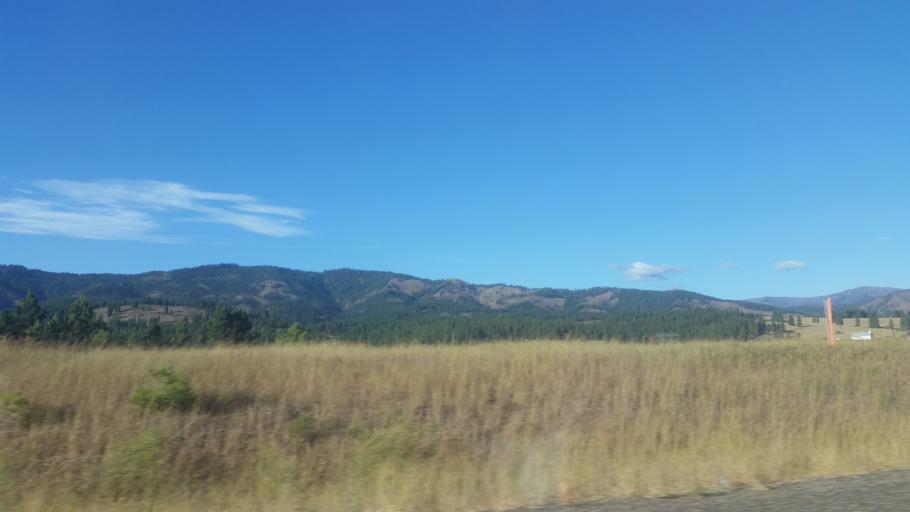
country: US
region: Washington
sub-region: Kittitas County
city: Cle Elum
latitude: 47.1958
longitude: -120.7722
